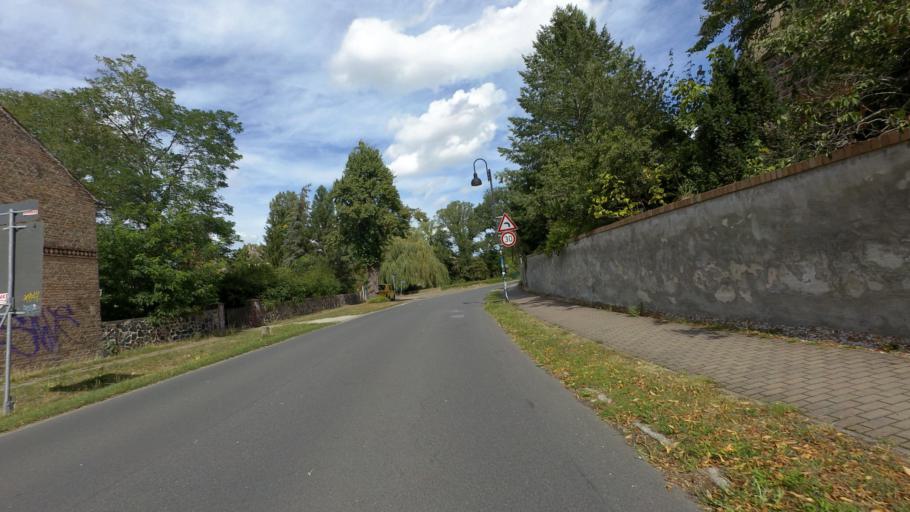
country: DE
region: Brandenburg
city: Gross Kreutz
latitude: 52.4046
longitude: 12.7764
